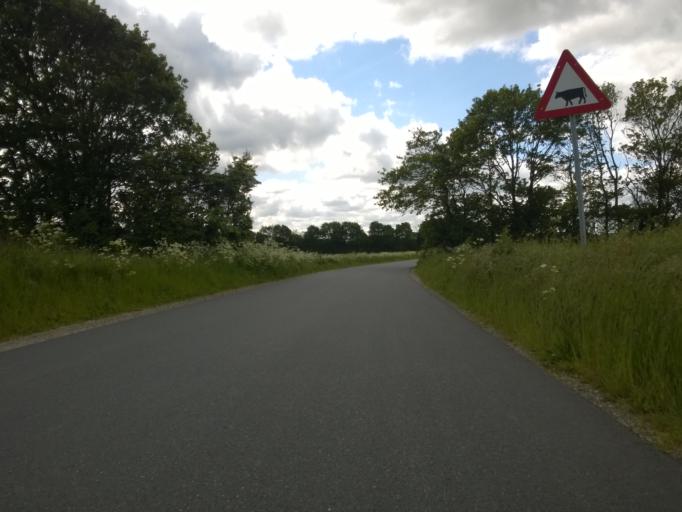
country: DK
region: Central Jutland
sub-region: Holstebro Kommune
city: Vinderup
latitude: 56.4038
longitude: 8.7796
